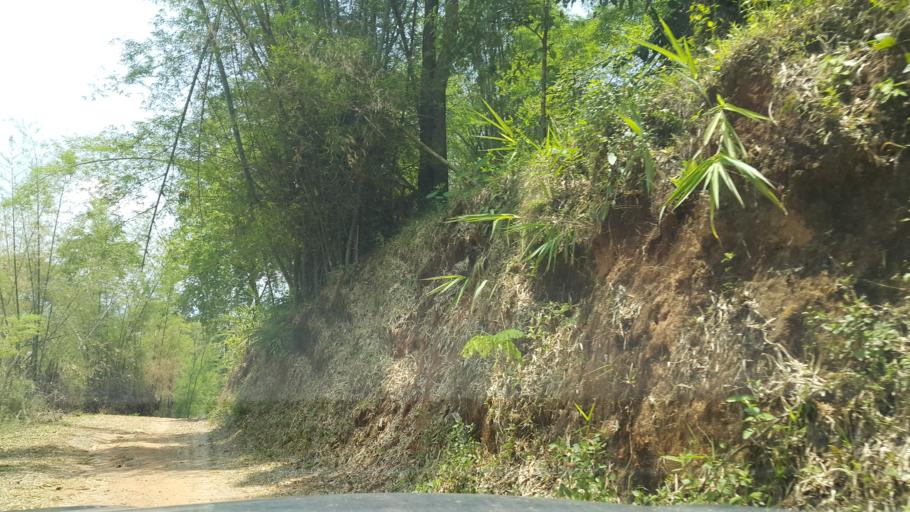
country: TH
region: Chiang Rai
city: Chiang Rai
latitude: 19.9985
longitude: 99.7105
